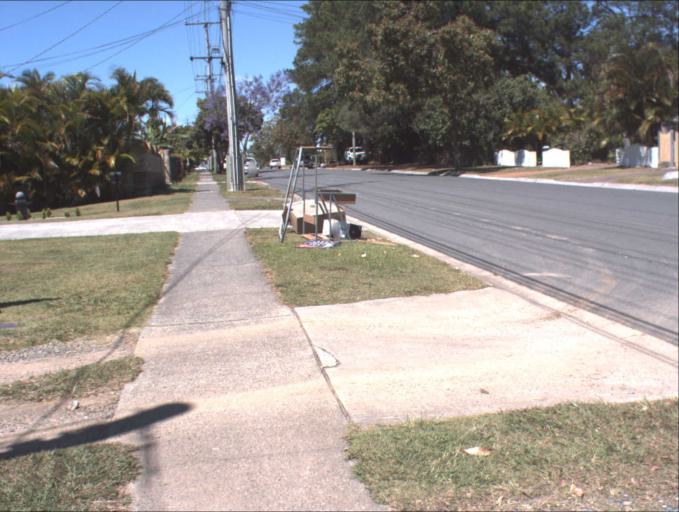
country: AU
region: Queensland
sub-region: Logan
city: Logan City
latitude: -27.6372
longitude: 153.1251
